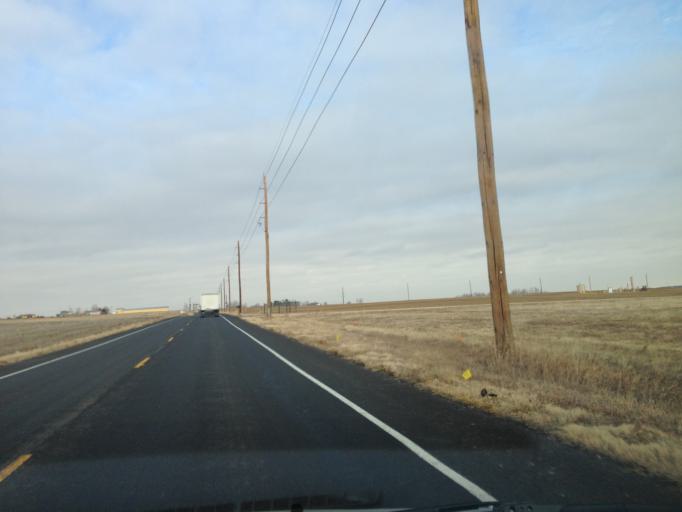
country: US
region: Colorado
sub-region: Boulder County
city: Lafayette
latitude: 40.0102
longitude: -105.0745
